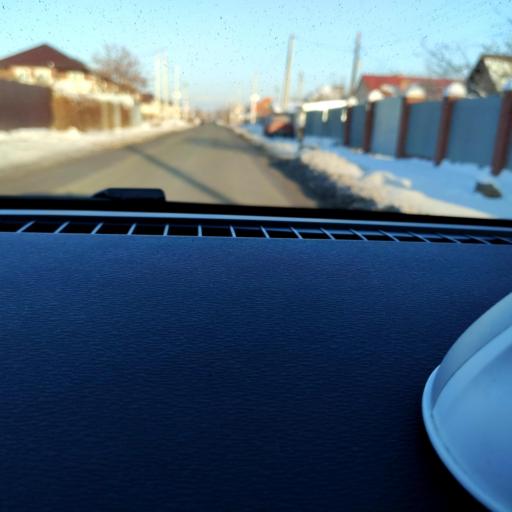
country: RU
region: Samara
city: Samara
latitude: 53.1342
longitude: 50.2384
